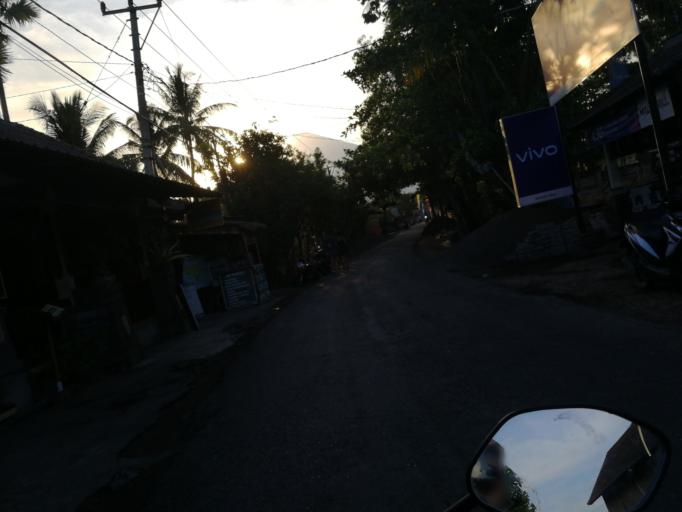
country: ID
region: Bali
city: Biaslantang Kaler
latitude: -8.3357
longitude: 115.6483
